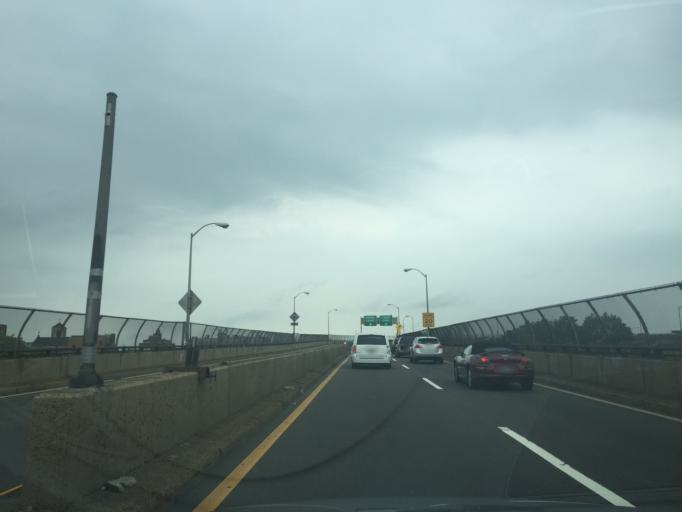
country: US
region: New York
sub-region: Kings County
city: Bensonhurst
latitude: 40.6122
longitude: -74.0314
